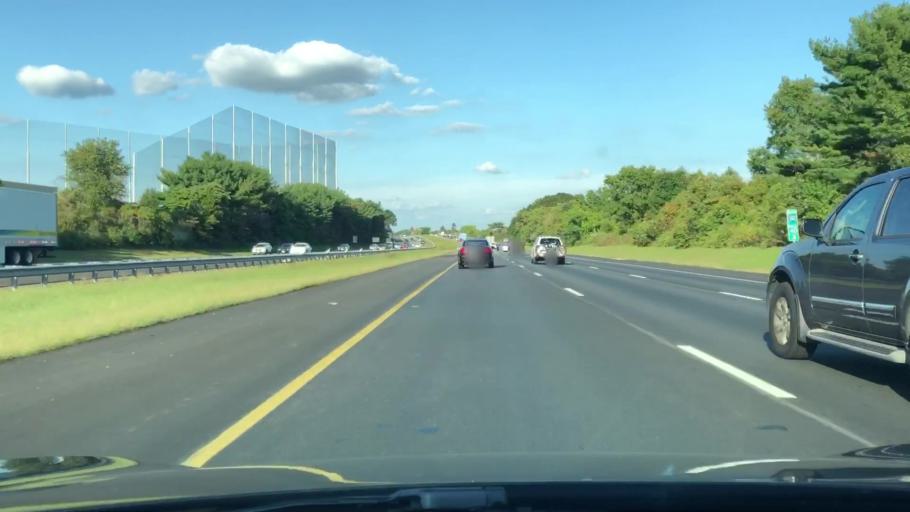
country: US
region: New Jersey
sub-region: Burlington County
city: Mount Laurel
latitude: 39.9705
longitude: -74.9066
